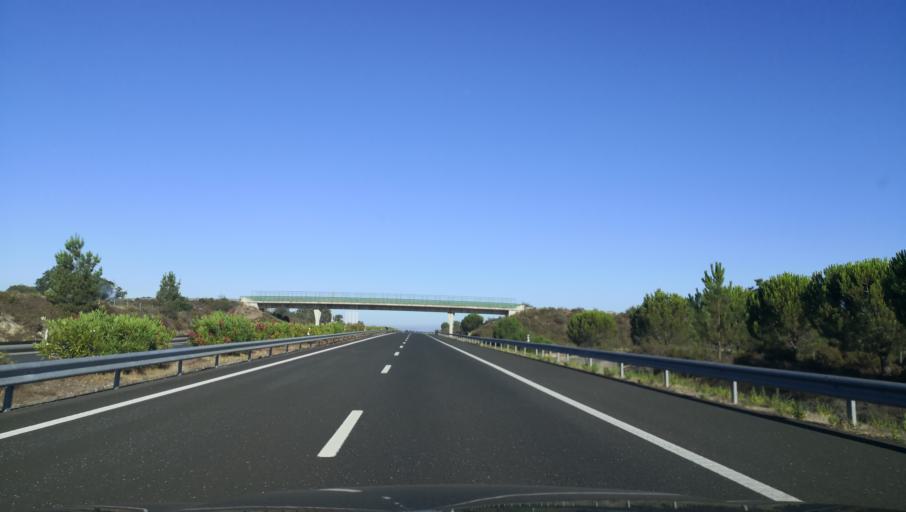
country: PT
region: Santarem
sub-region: Benavente
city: Poceirao
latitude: 38.8440
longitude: -8.7407
